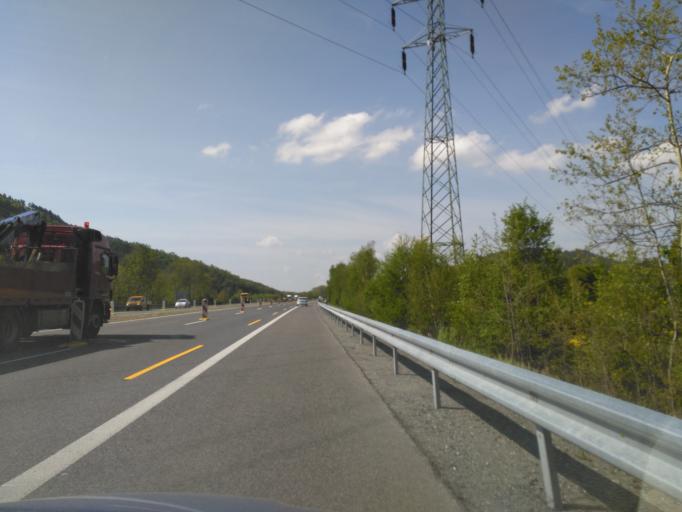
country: CZ
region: Central Bohemia
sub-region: Okres Beroun
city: Kraluv Dvur
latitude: 49.9255
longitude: 14.0104
